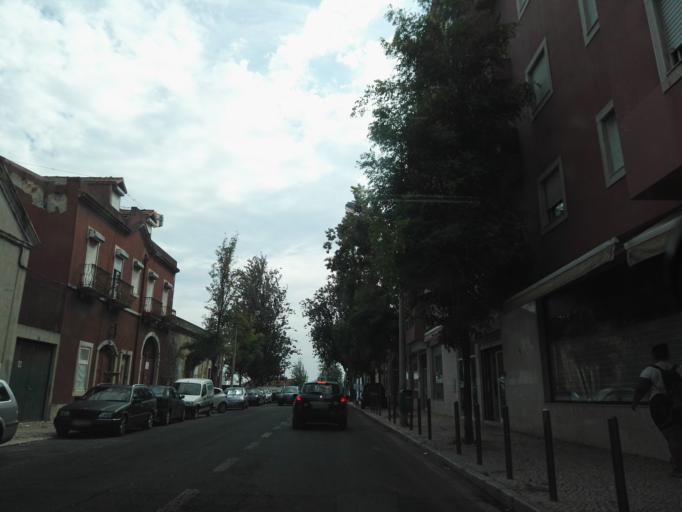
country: PT
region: Lisbon
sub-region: Loures
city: Moscavide
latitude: 38.7461
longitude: -9.1003
